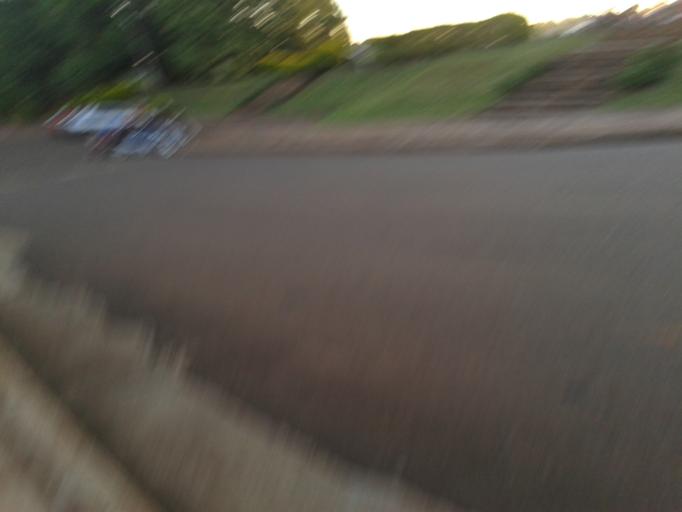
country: AR
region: Misiones
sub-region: Departamento de Capital
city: Posadas
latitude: -27.3960
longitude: -55.9651
